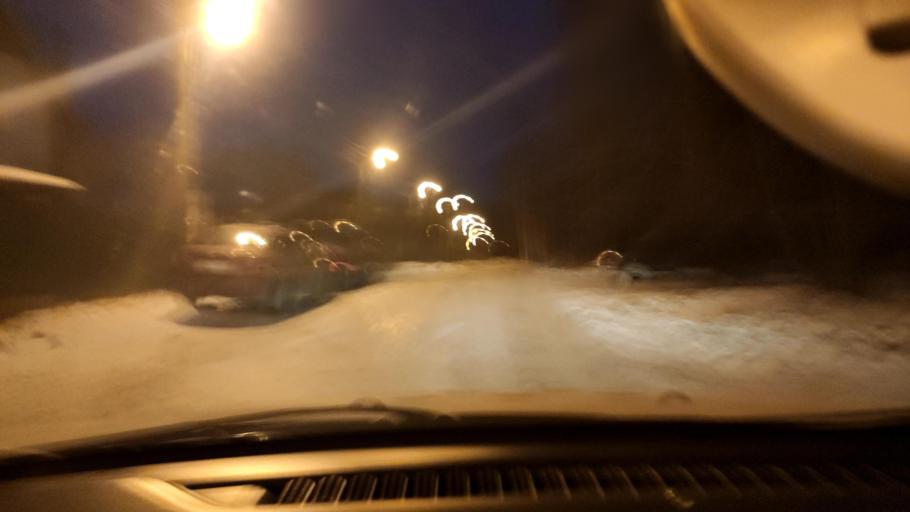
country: RU
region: Perm
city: Kondratovo
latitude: 58.0475
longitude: 56.1098
